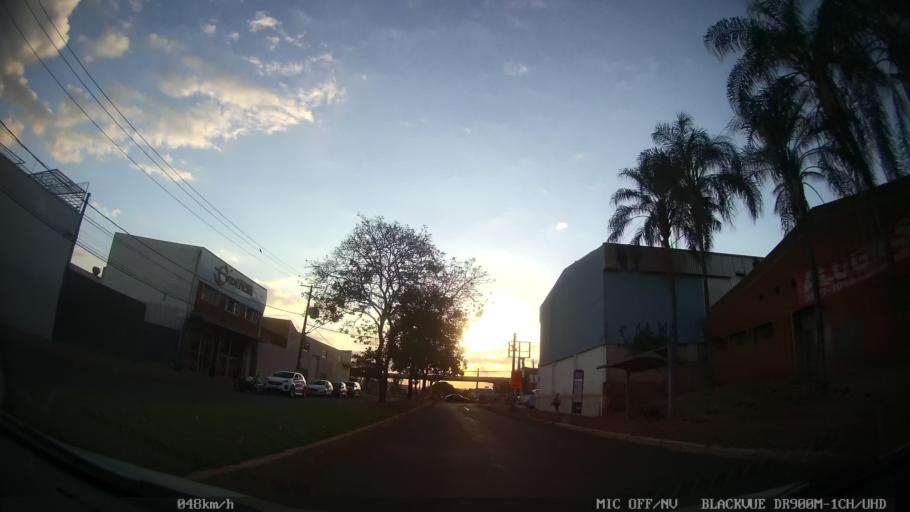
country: BR
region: Sao Paulo
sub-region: Ribeirao Preto
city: Ribeirao Preto
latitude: -21.1474
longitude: -47.7882
